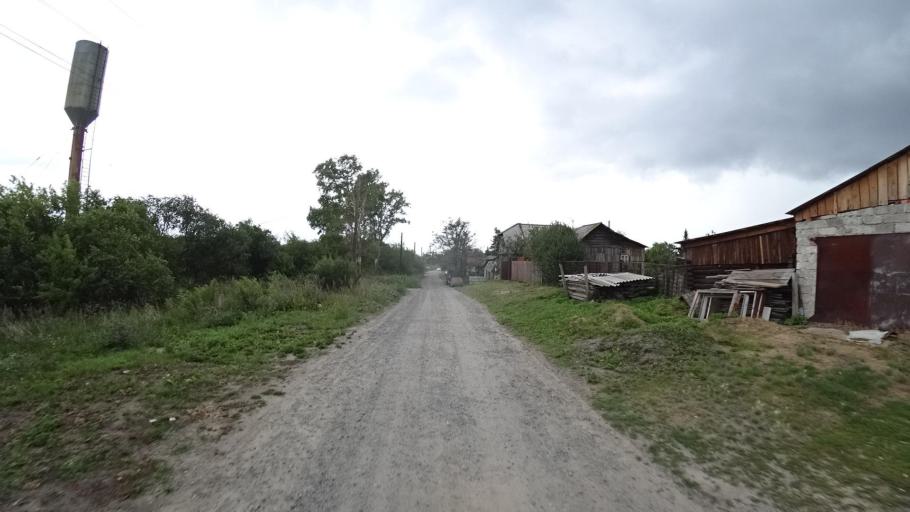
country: RU
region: Sverdlovsk
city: Kamyshlov
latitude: 56.8493
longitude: 62.6755
